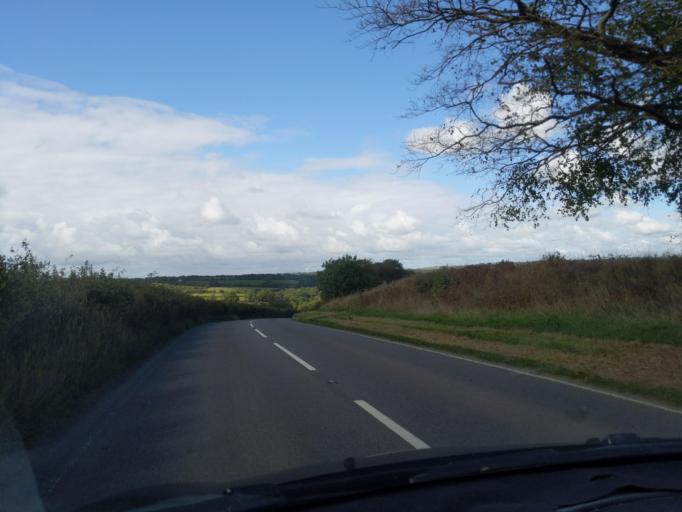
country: GB
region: England
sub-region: Devon
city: Holsworthy
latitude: 50.7627
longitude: -4.3351
